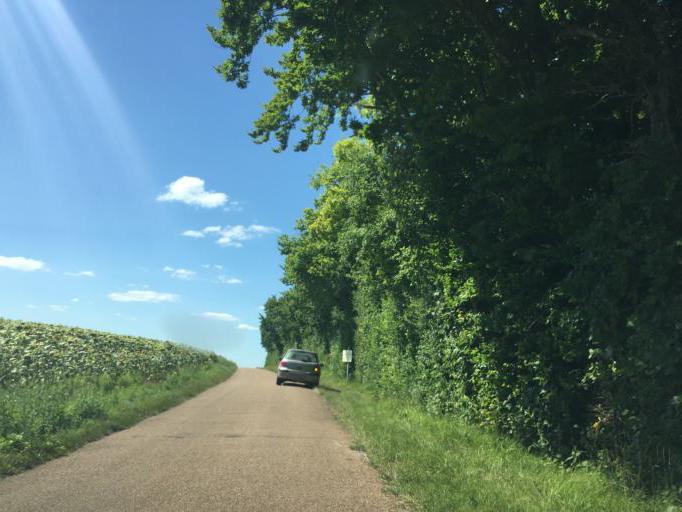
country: FR
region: Bourgogne
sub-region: Departement de l'Yonne
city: Fontenailles
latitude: 47.5898
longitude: 3.3396
